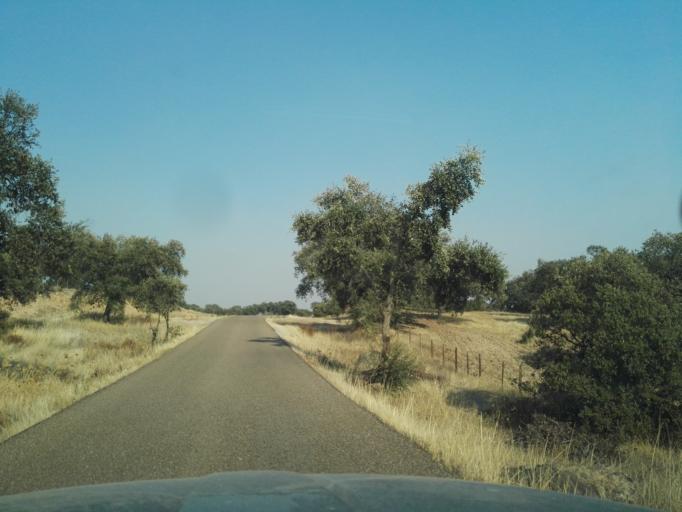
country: PT
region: Portalegre
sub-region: Campo Maior
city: Campo Maior
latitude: 38.9937
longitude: -7.1646
